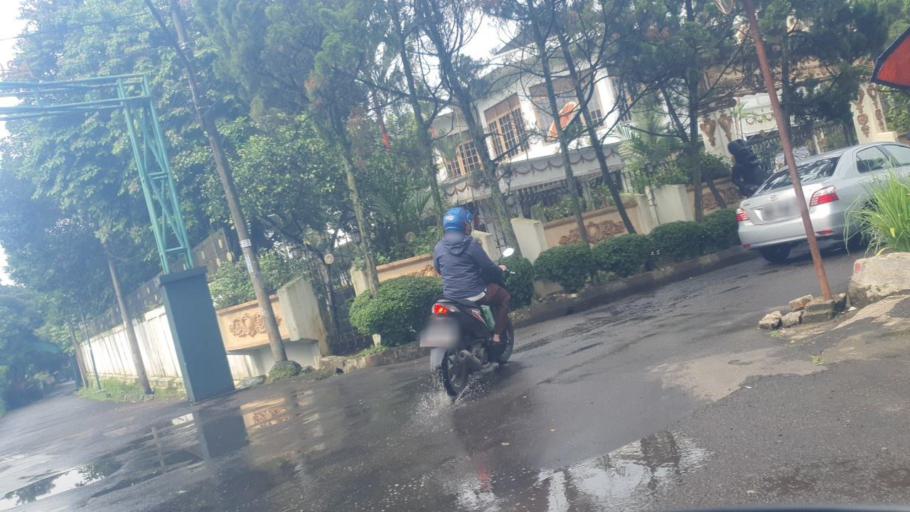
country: ID
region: West Java
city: Bogor
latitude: -6.5841
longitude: 106.8039
